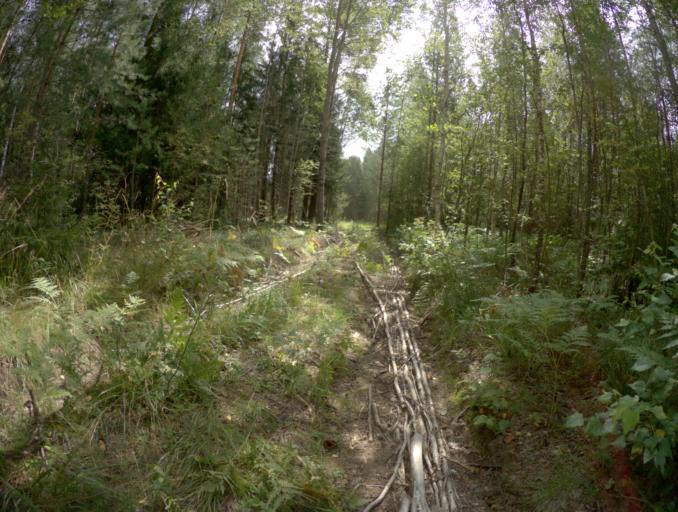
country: RU
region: Vladimir
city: Raduzhnyy
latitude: 55.9650
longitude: 40.2231
